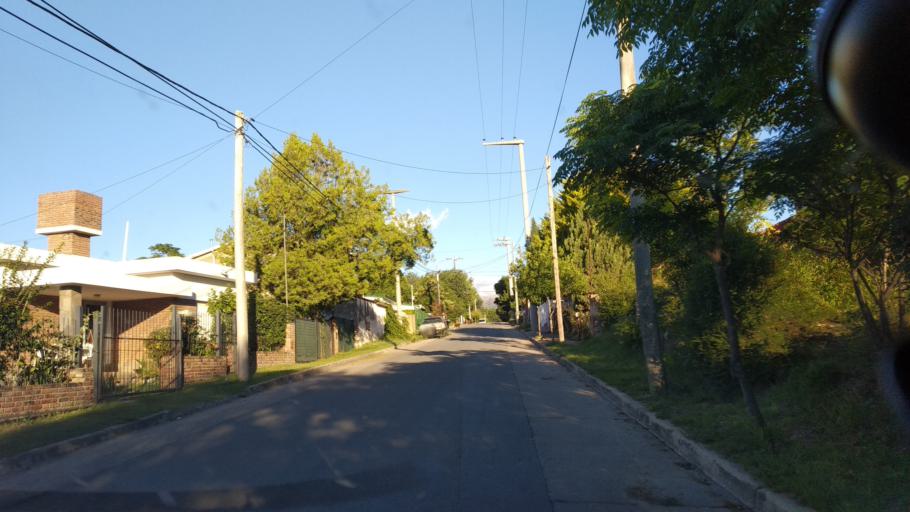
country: AR
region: Cordoba
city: Mina Clavero
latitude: -31.7153
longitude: -65.0050
